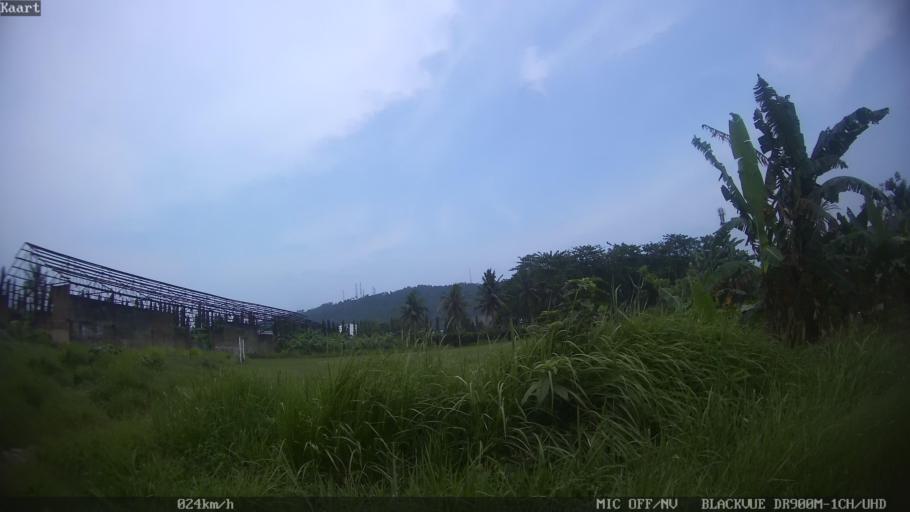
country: ID
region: Lampung
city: Panjang
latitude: -5.4337
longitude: 105.3271
